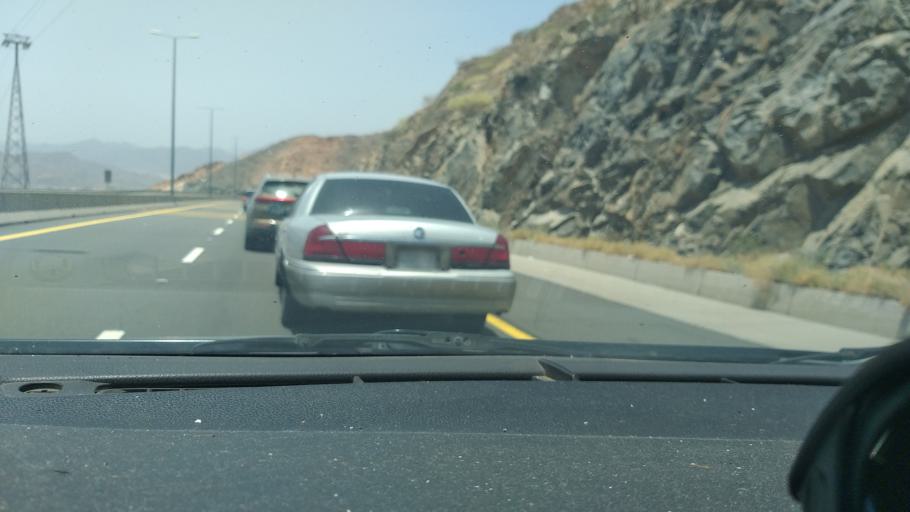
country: SA
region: Makkah
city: Al Hada
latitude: 21.3578
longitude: 40.2380
